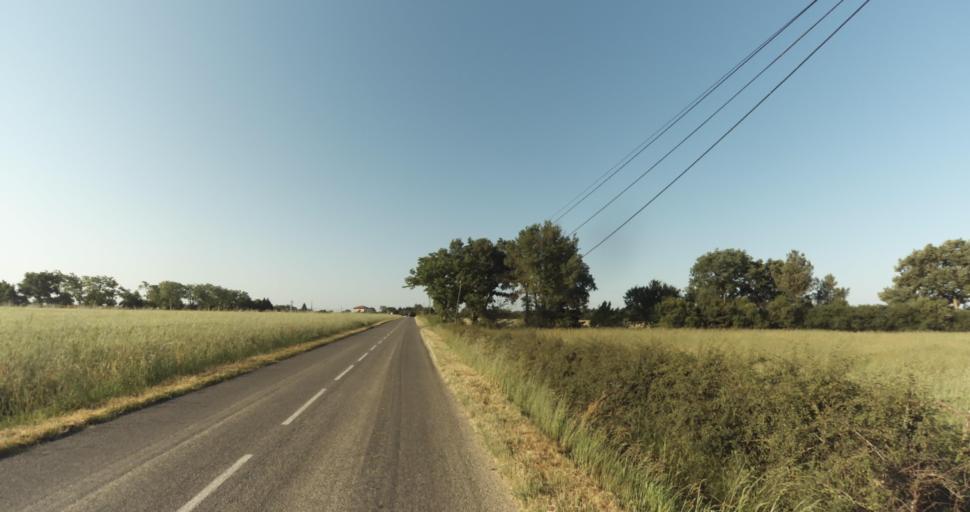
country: FR
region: Midi-Pyrenees
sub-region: Departement de la Haute-Garonne
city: Leguevin
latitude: 43.5790
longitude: 1.2362
